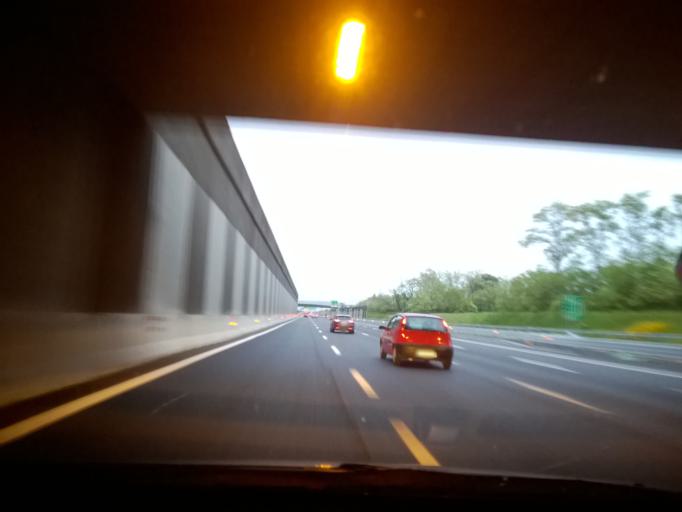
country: IT
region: Lombardy
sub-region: Citta metropolitana di Milano
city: Pregnana Milanese
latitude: 45.5065
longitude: 9.0036
